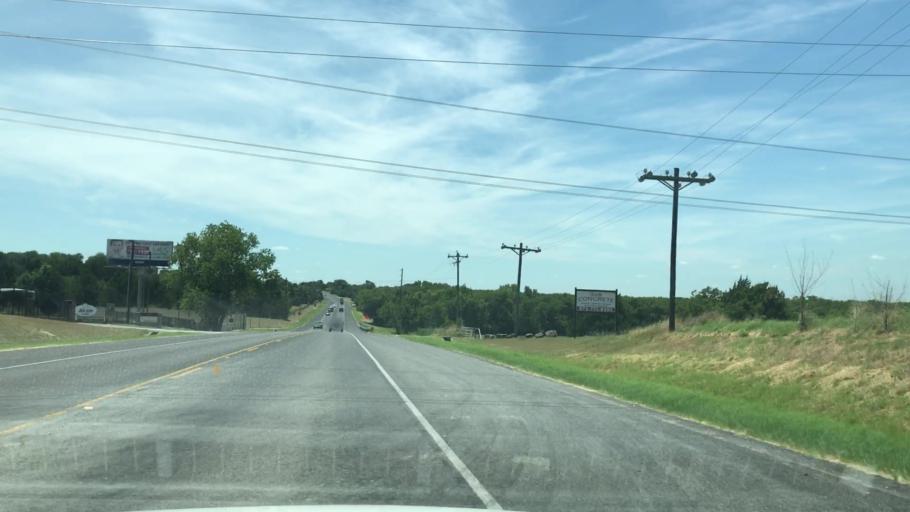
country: US
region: Texas
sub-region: Collin County
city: Lavon
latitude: 33.0043
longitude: -96.4620
